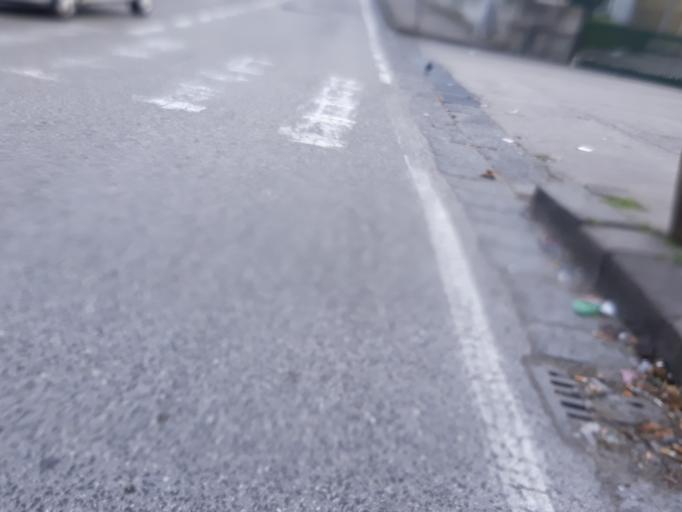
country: IT
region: Campania
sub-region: Provincia di Napoli
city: Napoli
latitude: 40.8610
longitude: 14.2814
